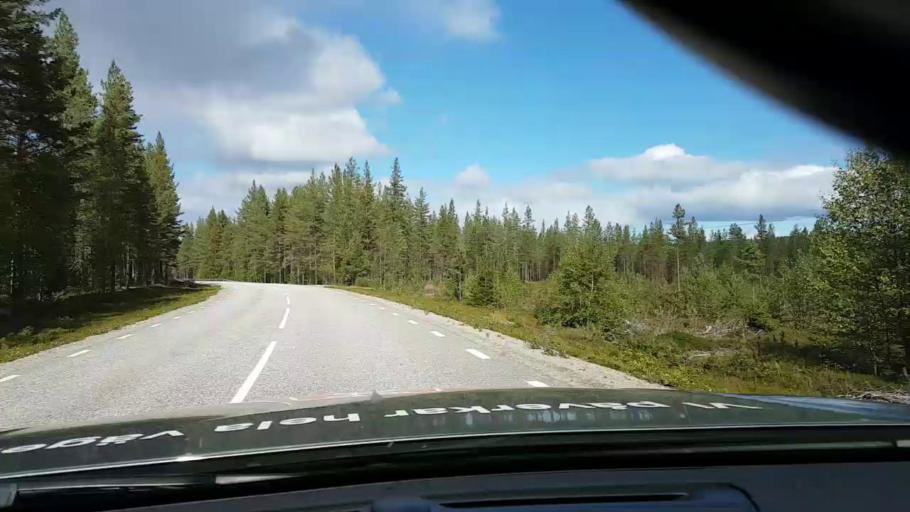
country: SE
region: Vaesternorrland
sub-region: OErnskoeldsviks Kommun
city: Bredbyn
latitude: 63.6891
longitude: 17.7706
